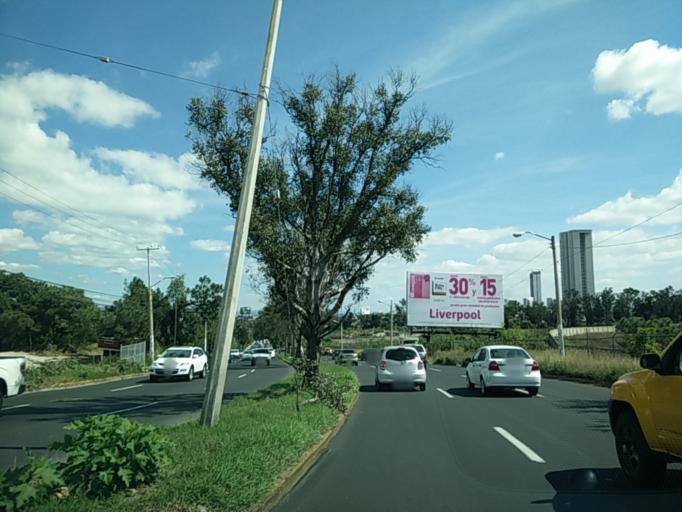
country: MX
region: Jalisco
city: Zapopan2
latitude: 20.7208
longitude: -103.4294
